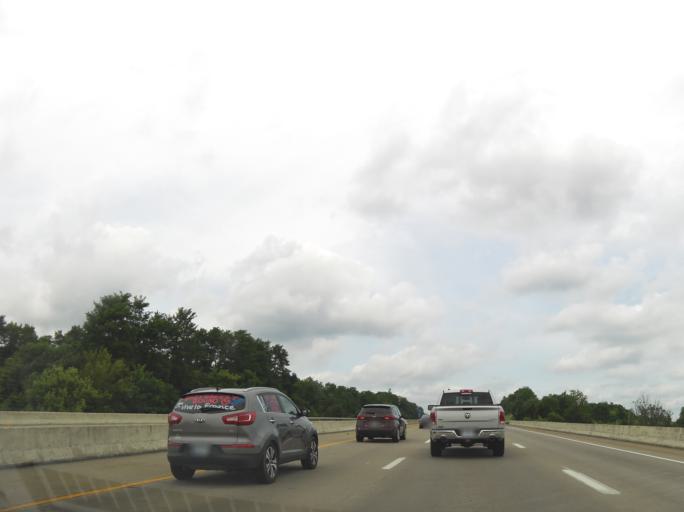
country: US
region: Kentucky
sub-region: Scott County
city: Georgetown
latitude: 38.3485
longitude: -84.5682
